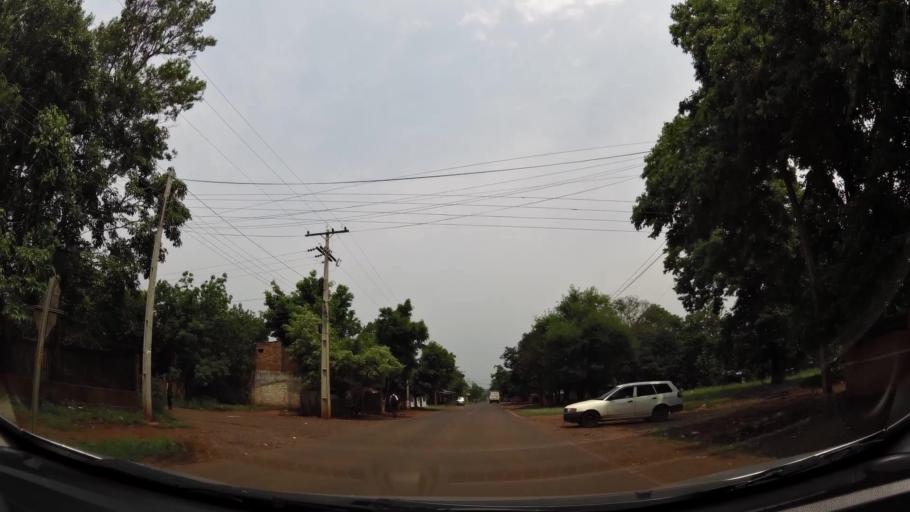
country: AR
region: Misiones
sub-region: Departamento de Iguazu
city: Puerto Iguazu
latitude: -25.5872
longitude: -54.6026
